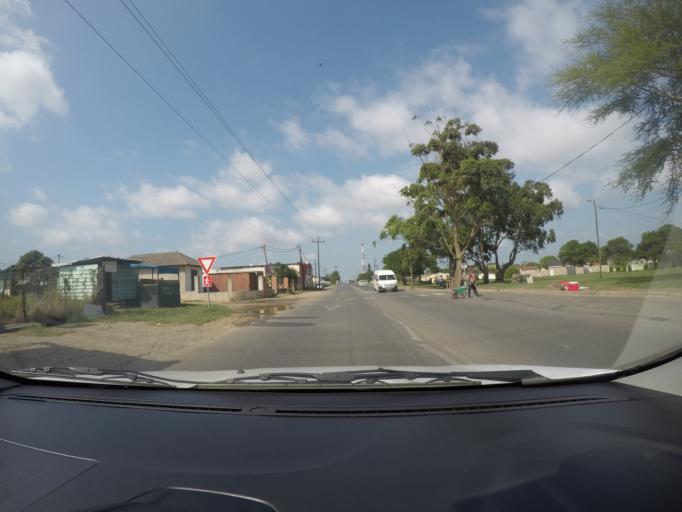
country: ZA
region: KwaZulu-Natal
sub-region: uThungulu District Municipality
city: eSikhawini
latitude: -28.8735
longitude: 31.9184
